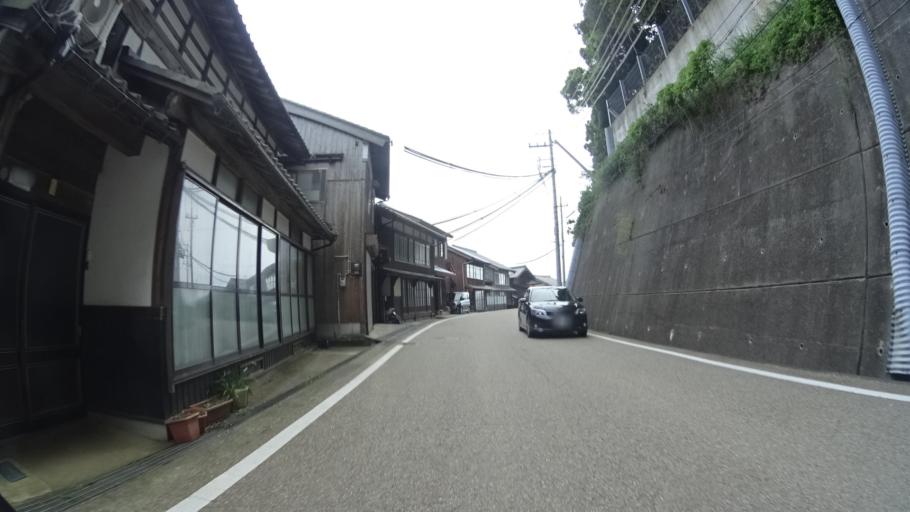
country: JP
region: Kyoto
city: Miyazu
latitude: 35.6701
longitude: 135.2831
